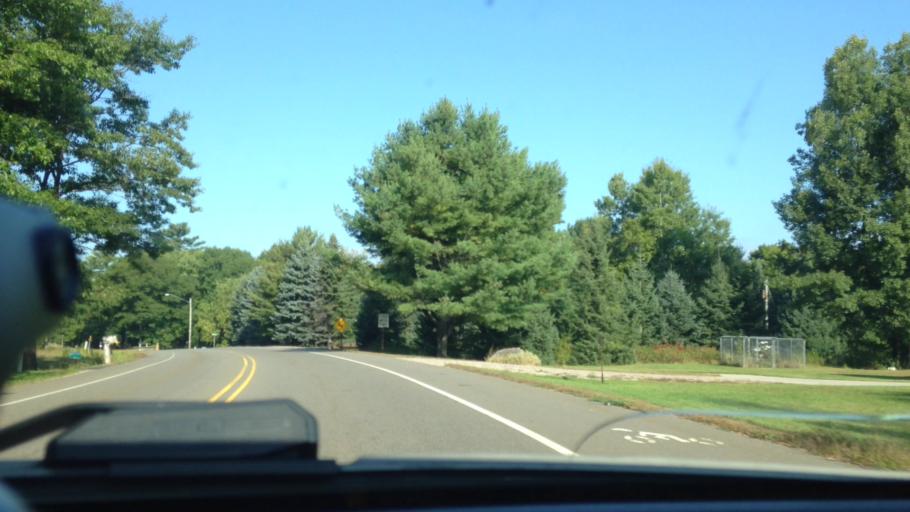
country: US
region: Michigan
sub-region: Dickinson County
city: Quinnesec
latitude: 45.8284
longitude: -87.9937
